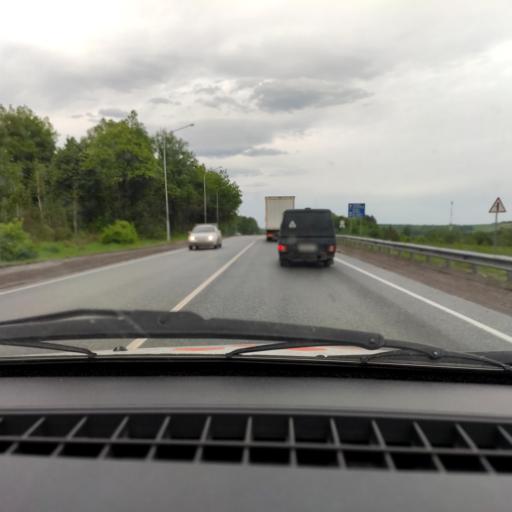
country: RU
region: Bashkortostan
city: Iglino
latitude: 54.7632
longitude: 56.4091
